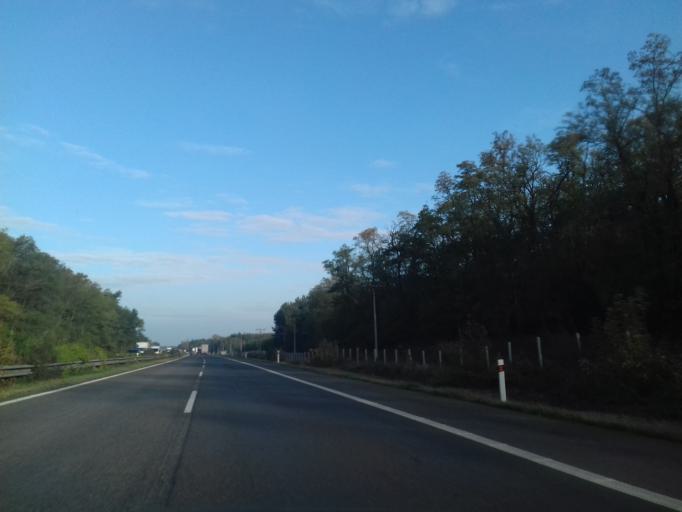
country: SK
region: Bratislavsky
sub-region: Okres Malacky
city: Malacky
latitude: 48.4515
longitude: 17.0412
